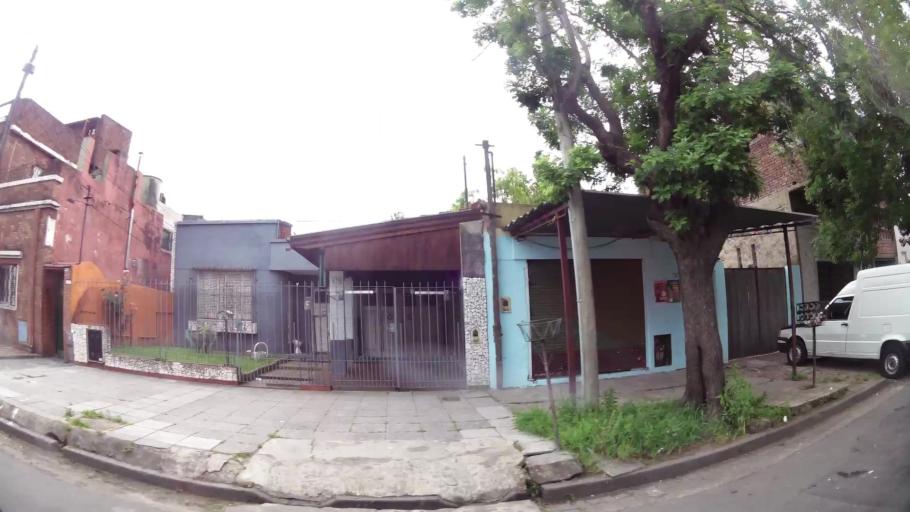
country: AR
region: Buenos Aires
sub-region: Partido de Avellaneda
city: Avellaneda
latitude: -34.6604
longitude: -58.3520
